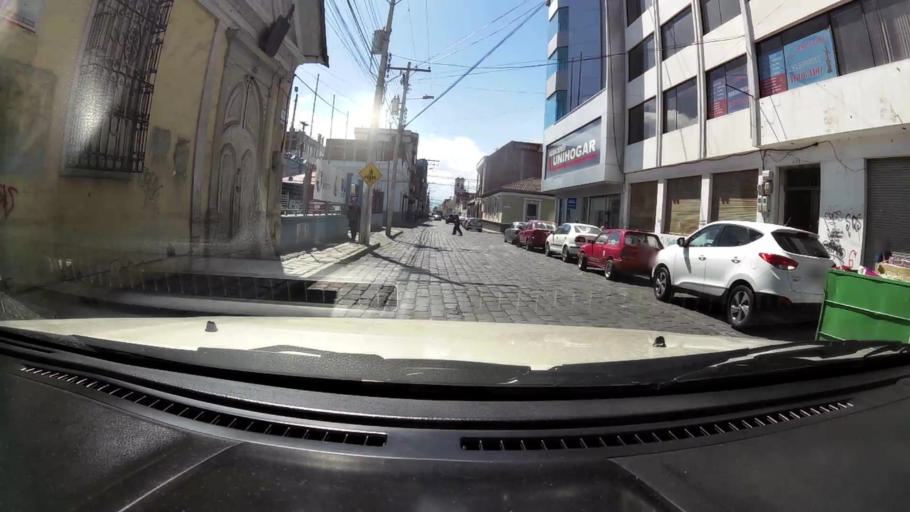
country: EC
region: Chimborazo
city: Riobamba
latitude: -1.6695
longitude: -78.6514
